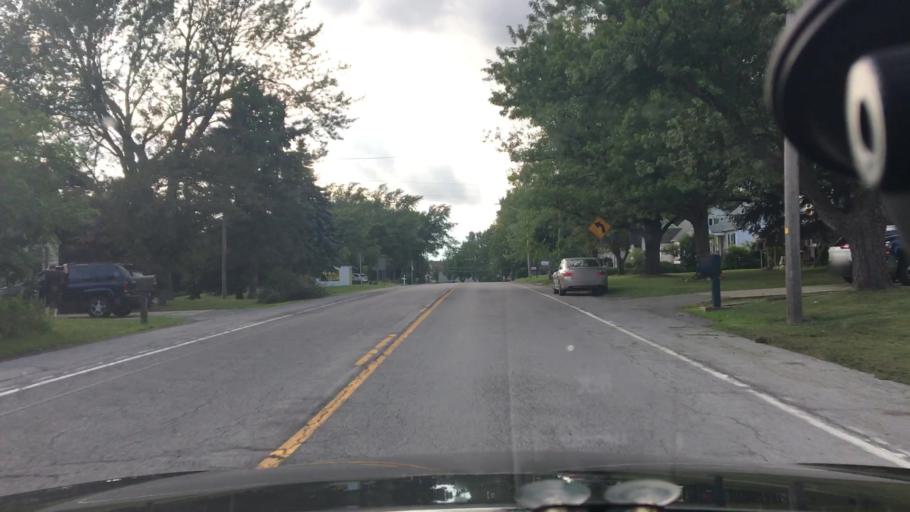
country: US
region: New York
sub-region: Erie County
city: Depew
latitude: 42.8377
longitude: -78.7172
